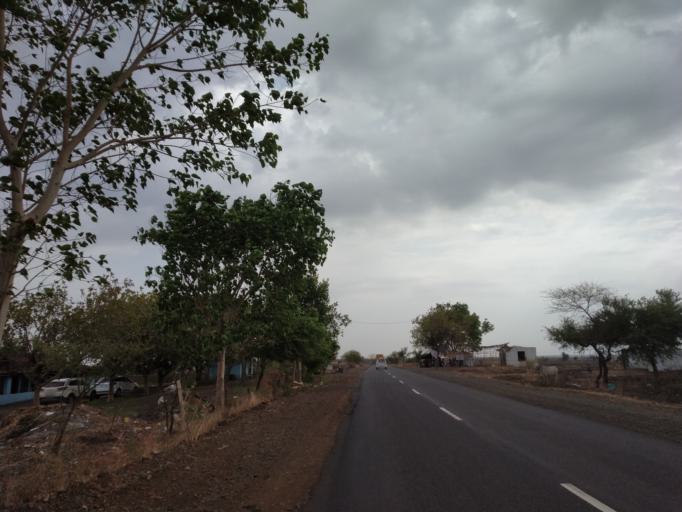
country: IN
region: Madhya Pradesh
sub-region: Shajapur
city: Susner
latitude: 24.0344
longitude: 76.1411
